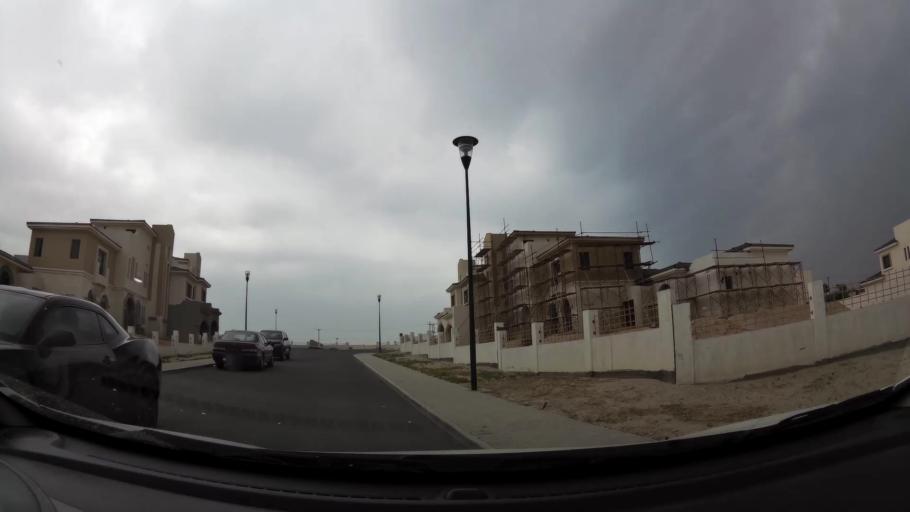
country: BH
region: Northern
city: Ar Rifa'
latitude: 26.0825
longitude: 50.5556
